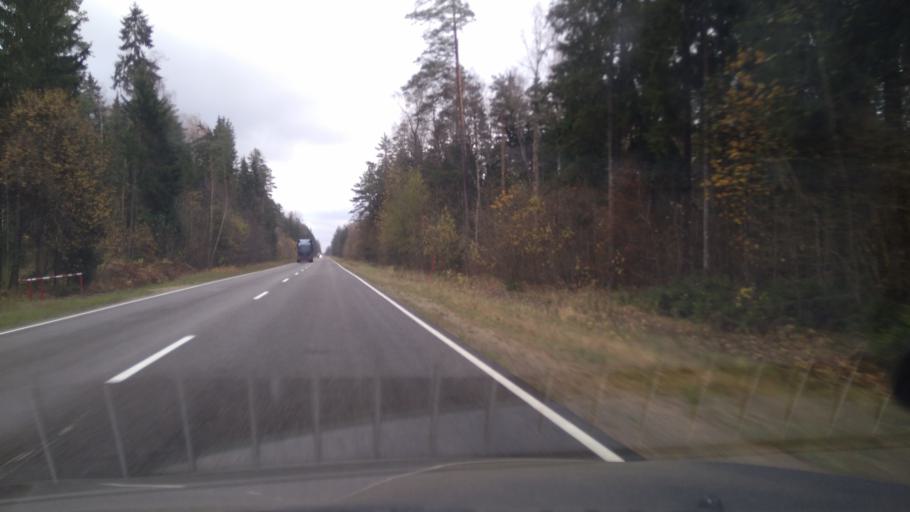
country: BY
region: Minsk
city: Urechcha
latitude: 53.2138
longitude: 27.8690
